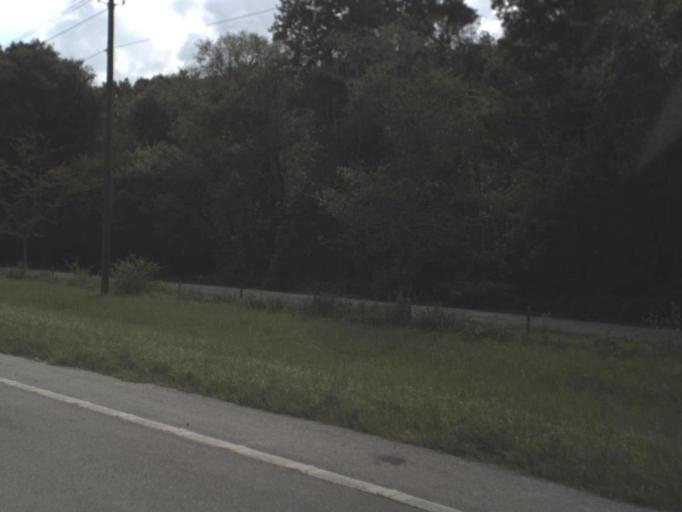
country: US
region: Florida
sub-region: Hillsborough County
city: Thonotosassa
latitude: 28.0835
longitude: -82.2750
